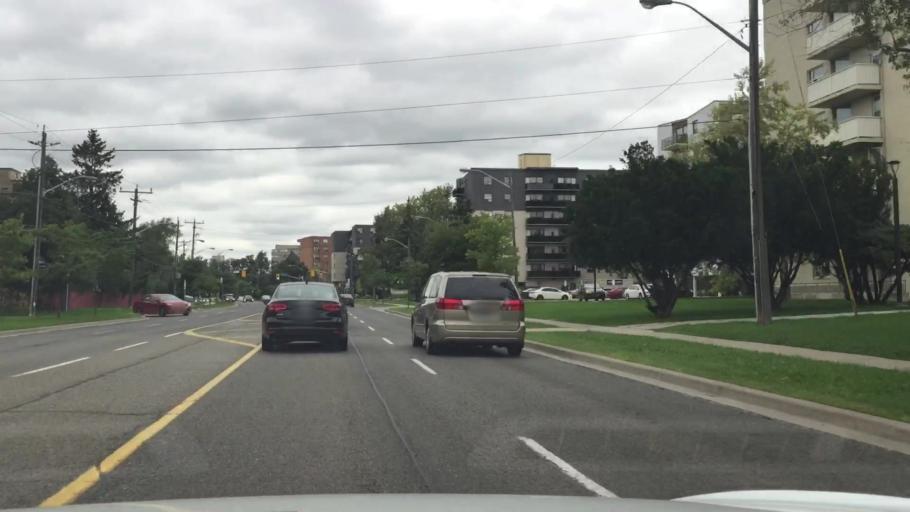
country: CA
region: Ontario
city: Scarborough
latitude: 43.7589
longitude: -79.3203
